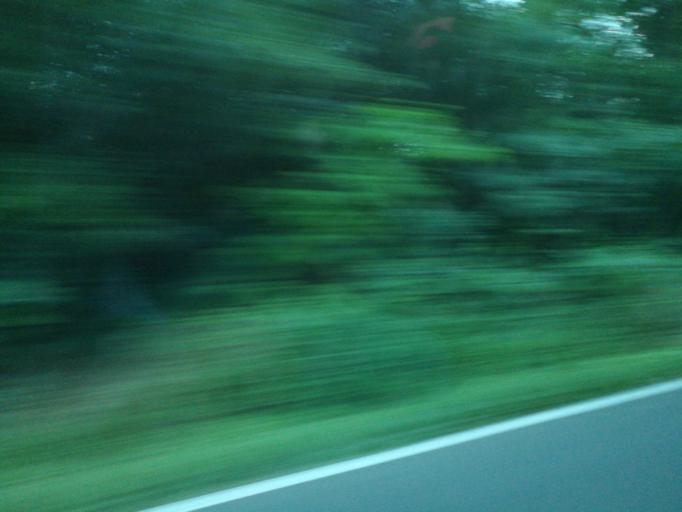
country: RO
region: Constanta
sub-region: Comuna Douazeci si Trei August
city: Douazeci si Trei August
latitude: 43.8591
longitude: 28.5887
